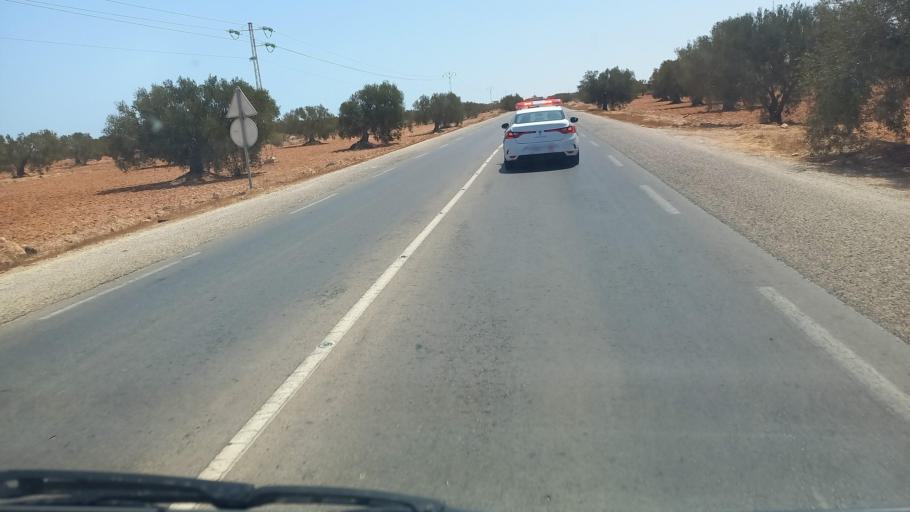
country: TN
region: Madanin
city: Zarzis
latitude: 33.5567
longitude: 11.0596
